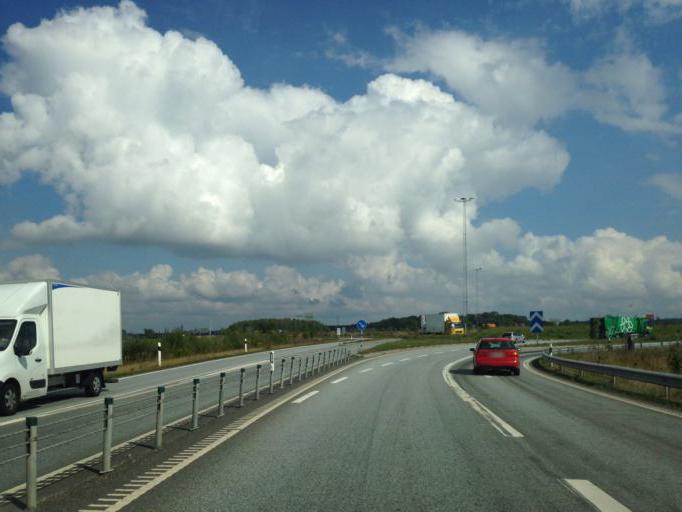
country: SE
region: Skane
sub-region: Staffanstorps Kommun
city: Hjaerup
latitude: 55.6946
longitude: 13.1317
